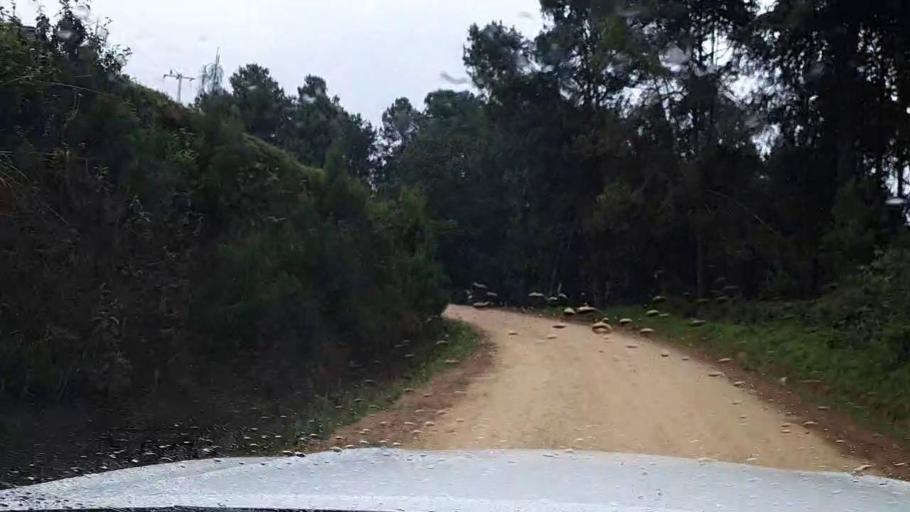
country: RW
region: Southern Province
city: Nzega
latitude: -2.3681
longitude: 29.3802
